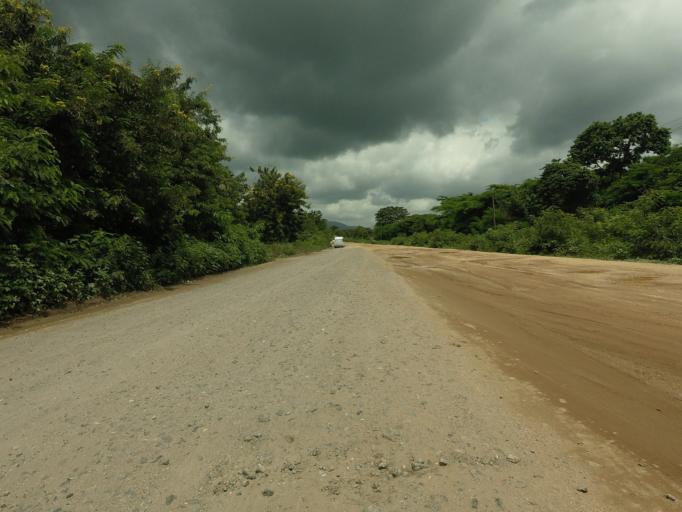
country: GH
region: Volta
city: Ho
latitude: 6.6460
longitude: 0.2987
